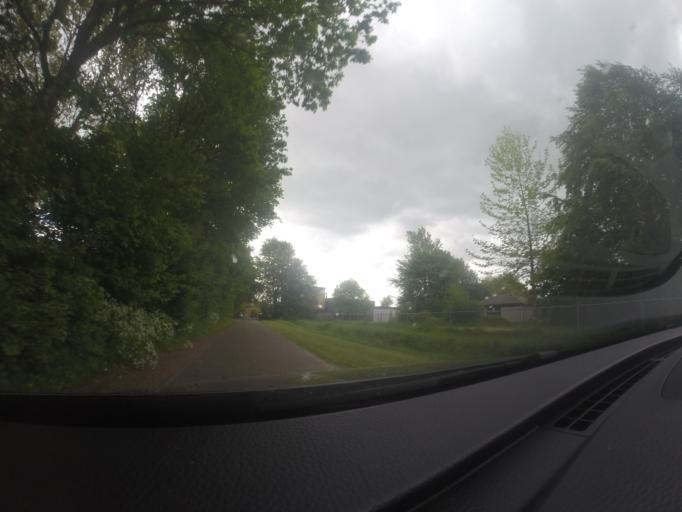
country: NL
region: Gelderland
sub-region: Gemeente Brummen
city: Brummen
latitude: 52.0962
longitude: 6.1487
